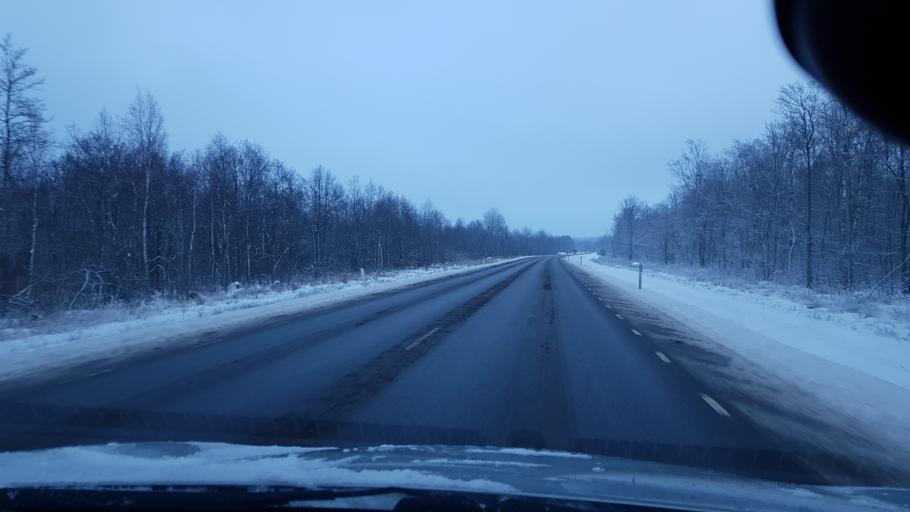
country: EE
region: Harju
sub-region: Paldiski linn
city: Paldiski
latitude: 59.3399
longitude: 24.1382
